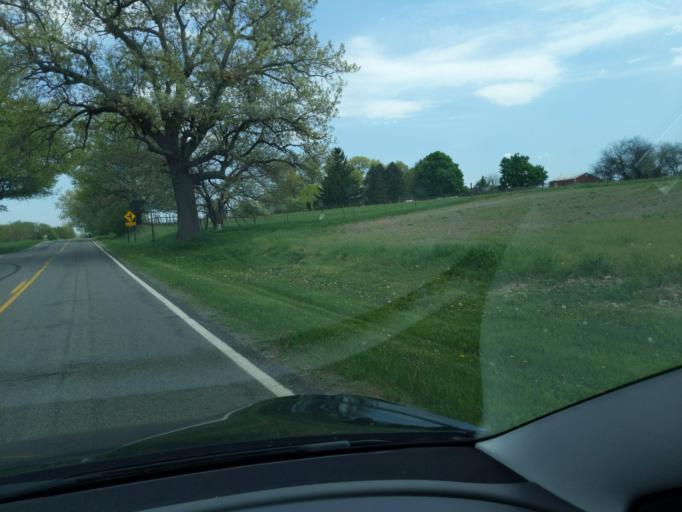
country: US
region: Michigan
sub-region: Ingham County
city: Stockbridge
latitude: 42.4899
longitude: -84.2950
